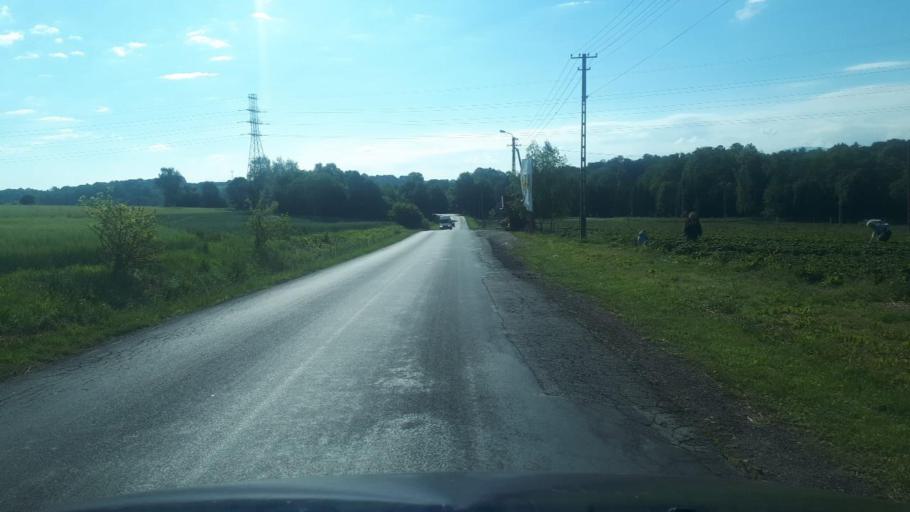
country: PL
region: Silesian Voivodeship
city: Janowice
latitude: 49.9072
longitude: 19.0993
